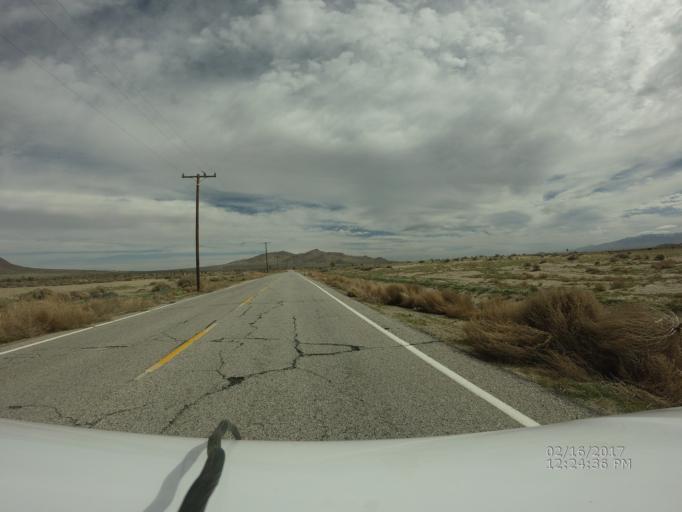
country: US
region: California
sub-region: Los Angeles County
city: Lake Los Angeles
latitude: 34.6753
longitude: -117.8505
